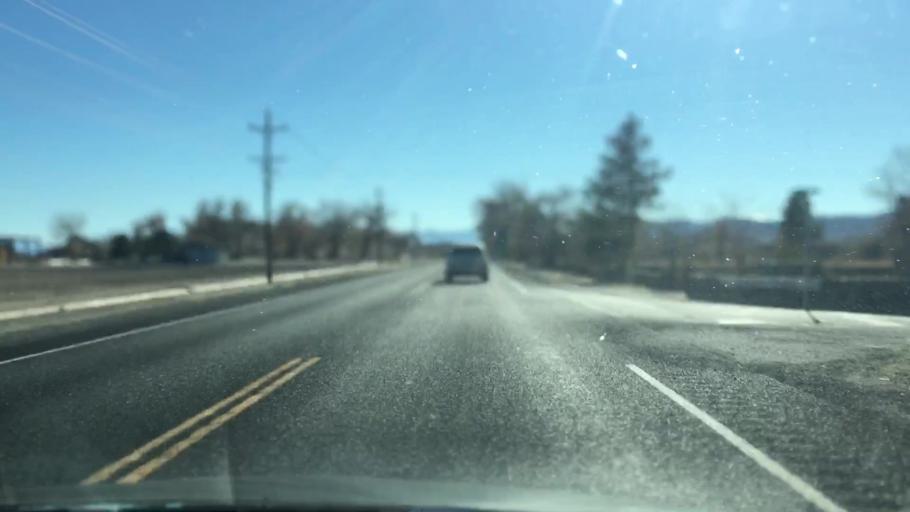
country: US
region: Nevada
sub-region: Lyon County
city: Yerington
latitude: 39.0341
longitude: -119.1816
